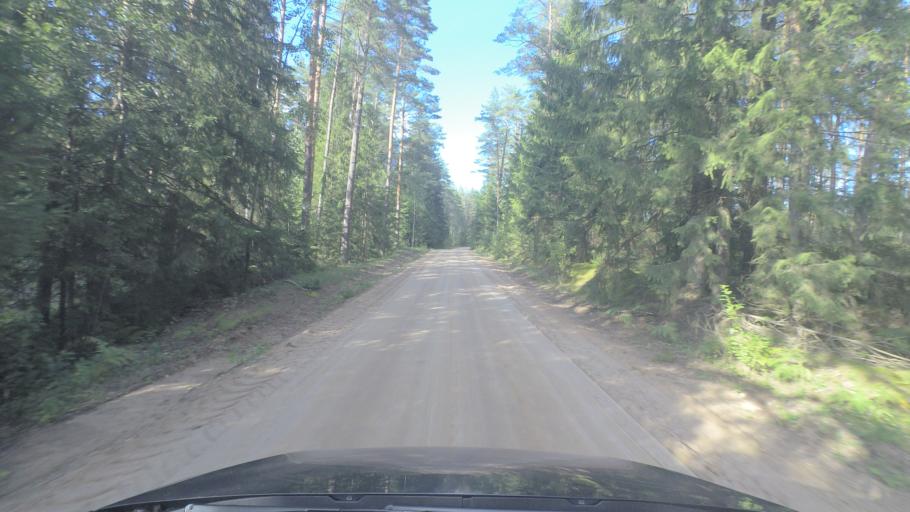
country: LT
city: Pabrade
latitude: 55.1638
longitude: 25.8291
